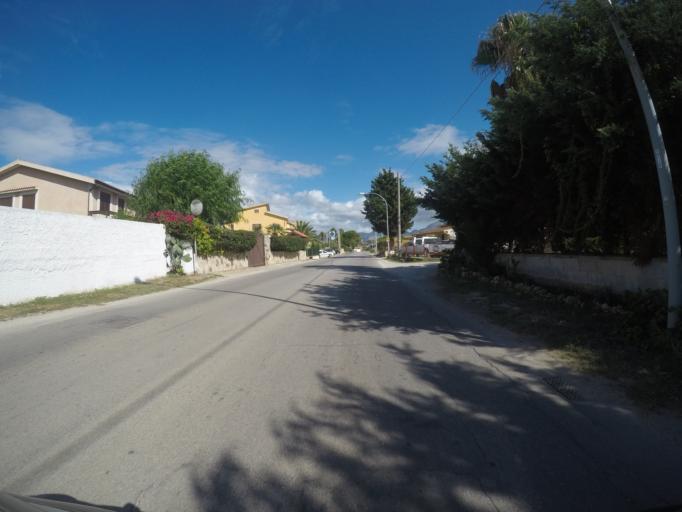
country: IT
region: Sicily
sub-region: Palermo
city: Trappeto
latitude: 38.0707
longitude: 13.0480
